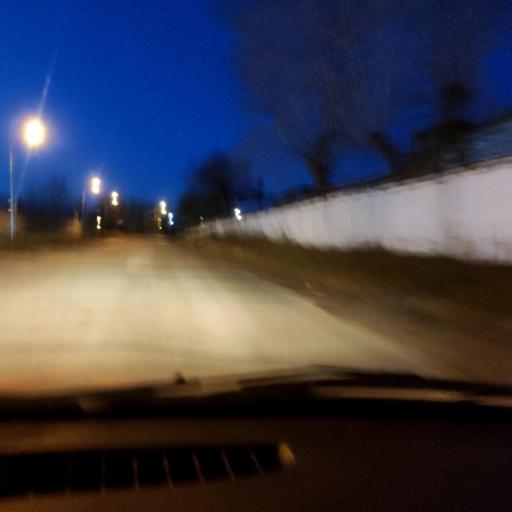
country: RU
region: Bashkortostan
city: Ufa
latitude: 54.8483
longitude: 56.0823
